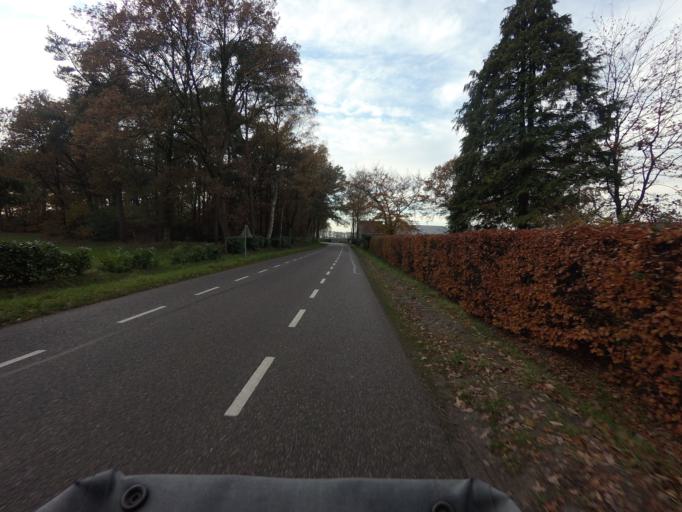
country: NL
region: North Brabant
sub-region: Gemeente Breda
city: Breda
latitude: 51.5015
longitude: 4.8112
